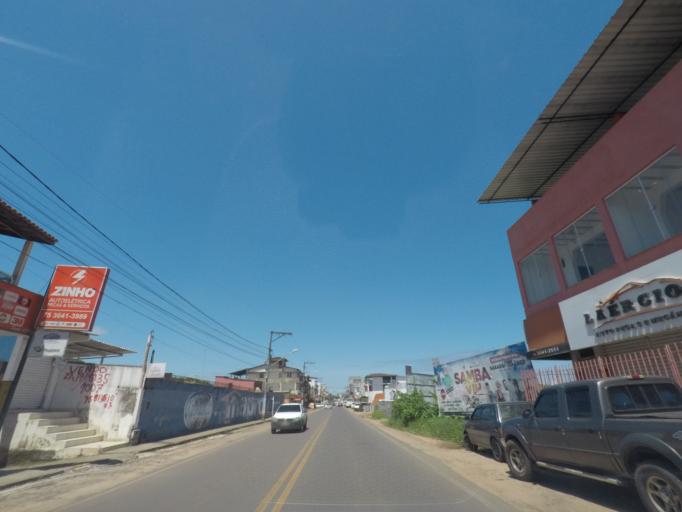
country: BR
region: Bahia
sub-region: Valenca
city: Valenca
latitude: -13.3585
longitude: -39.0650
